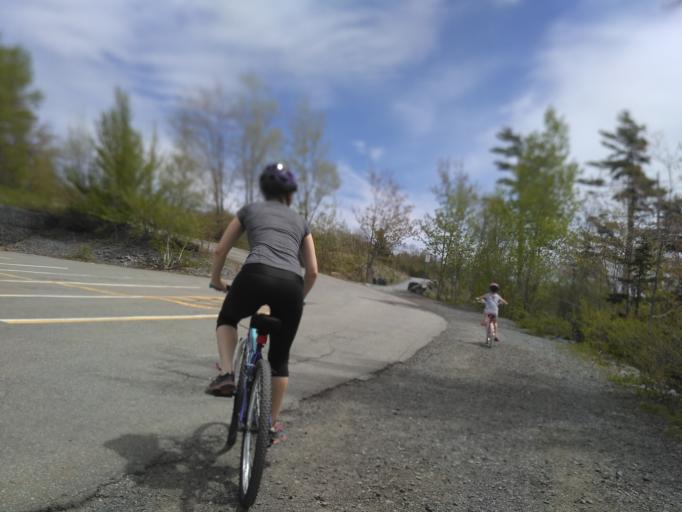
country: CA
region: Nova Scotia
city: Dartmouth
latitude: 44.7767
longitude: -63.6673
